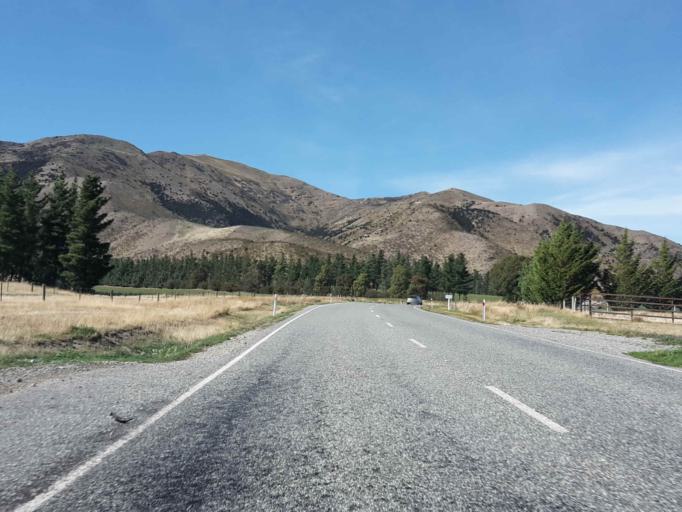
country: NZ
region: Otago
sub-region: Queenstown-Lakes District
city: Wanaka
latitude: -44.7436
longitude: 169.3386
